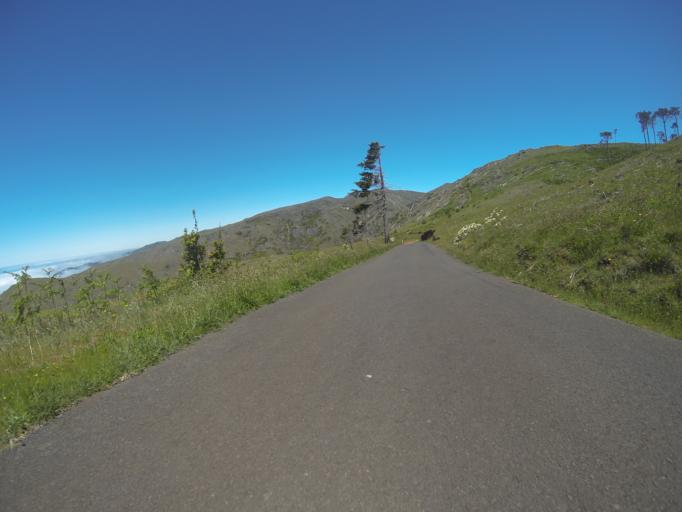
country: PT
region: Madeira
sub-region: Funchal
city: Nossa Senhora do Monte
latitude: 32.7077
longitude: -16.9136
